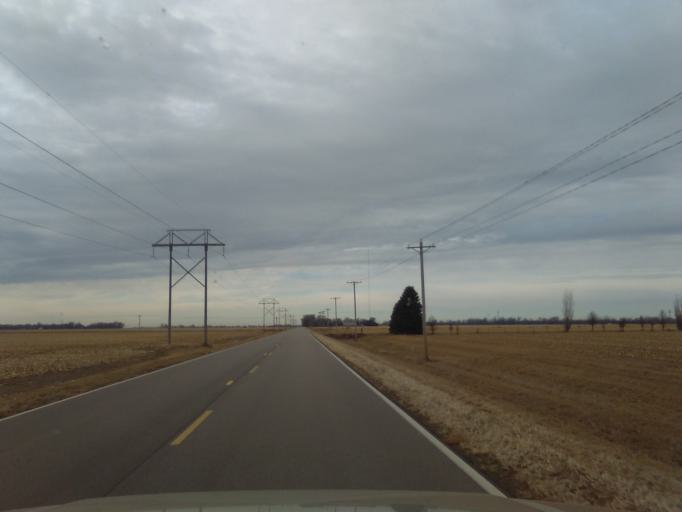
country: US
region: Nebraska
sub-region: Buffalo County
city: Gibbon
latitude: 40.6550
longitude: -98.8339
